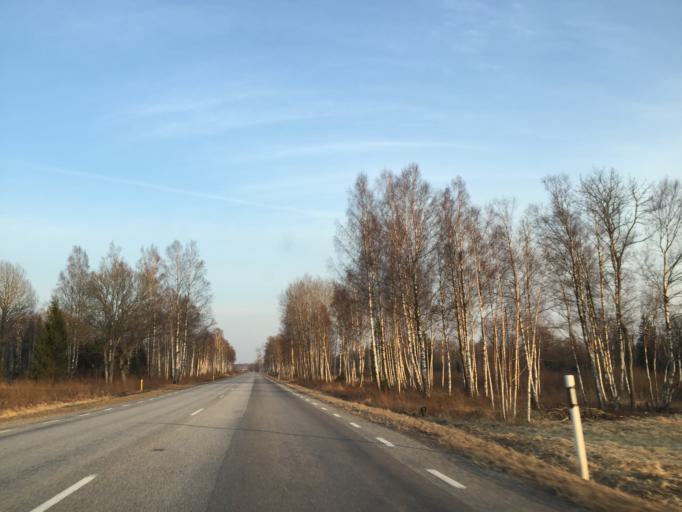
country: EE
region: Laeaene
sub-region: Lihula vald
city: Lihula
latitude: 58.5431
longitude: 24.0037
